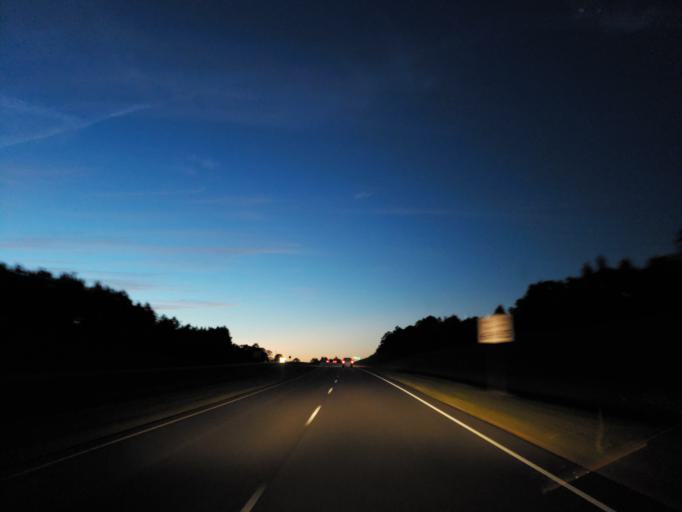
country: US
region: Mississippi
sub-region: Clarke County
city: Quitman
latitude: 32.1037
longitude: -88.7087
